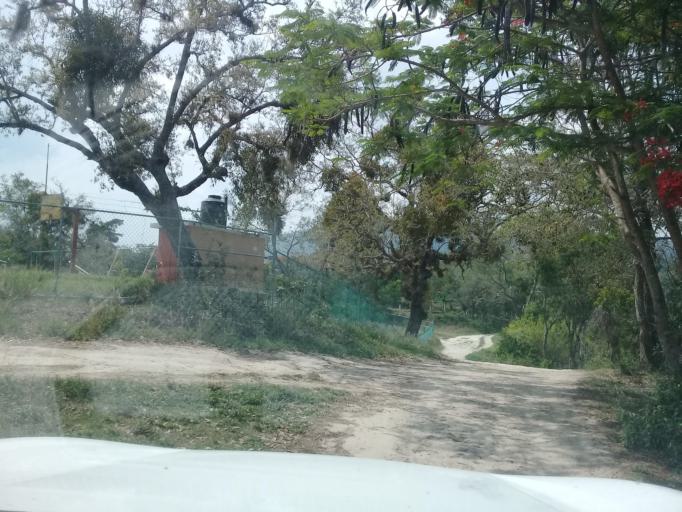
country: MX
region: Veracruz
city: Jalcomulco
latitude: 19.3883
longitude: -96.7916
